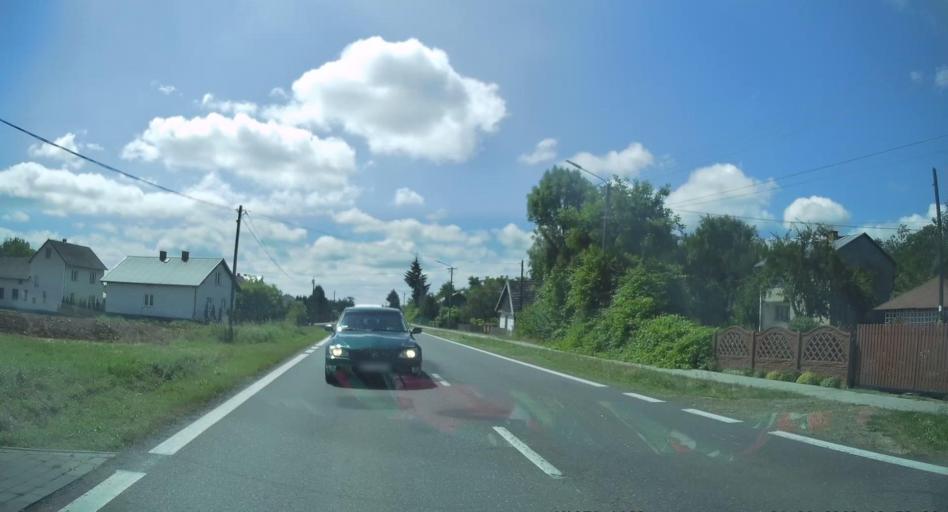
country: PL
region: Subcarpathian Voivodeship
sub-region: Powiat mielecki
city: Padew Narodowa
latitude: 50.4211
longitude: 21.4829
